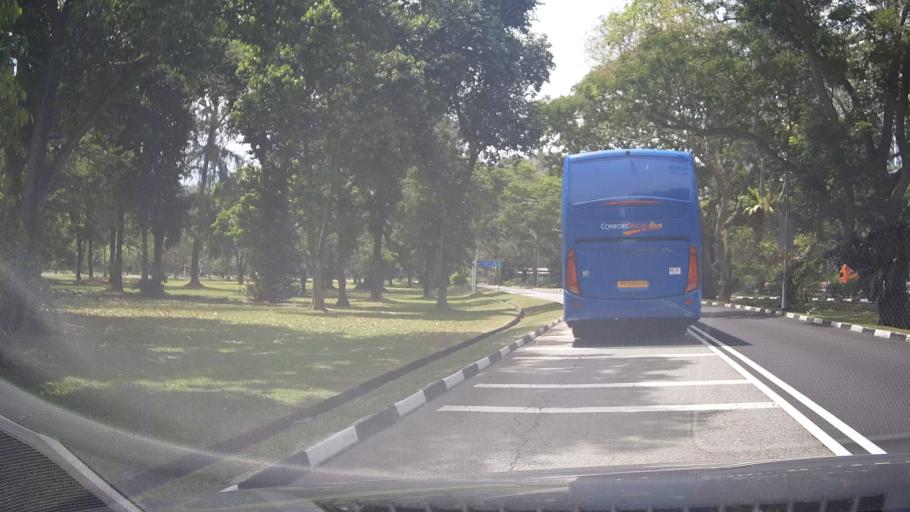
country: SG
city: Singapore
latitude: 1.2960
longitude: 103.8965
